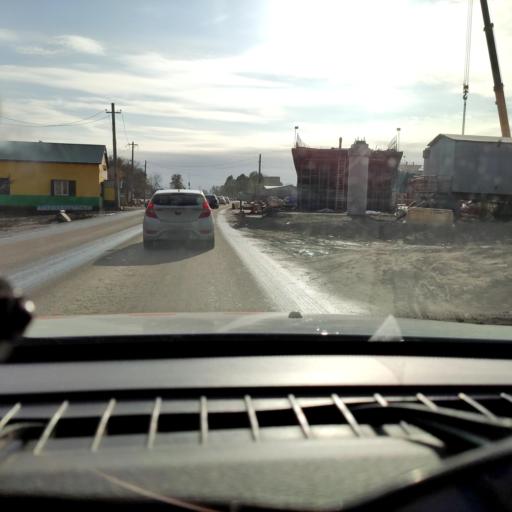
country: RU
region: Samara
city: Samara
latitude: 53.1372
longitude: 50.1035
